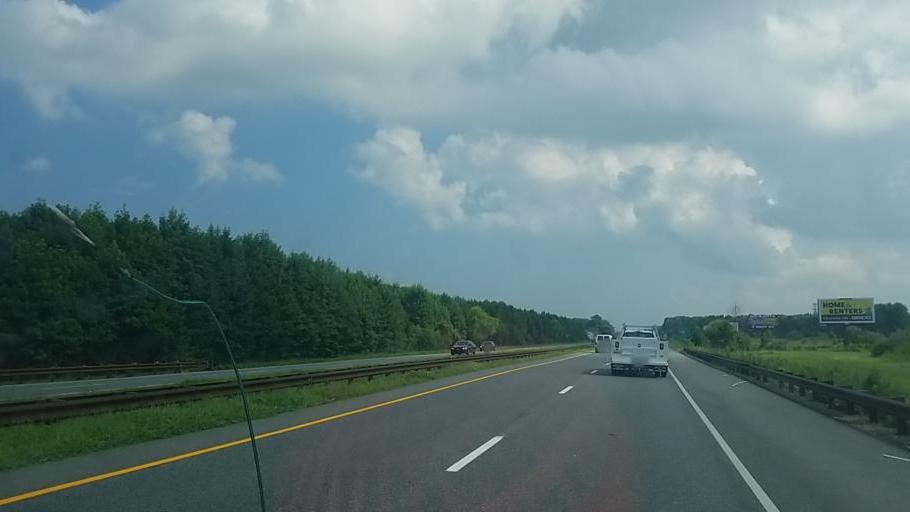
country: US
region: Delaware
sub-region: Sussex County
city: Selbyville
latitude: 38.4327
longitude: -75.2217
